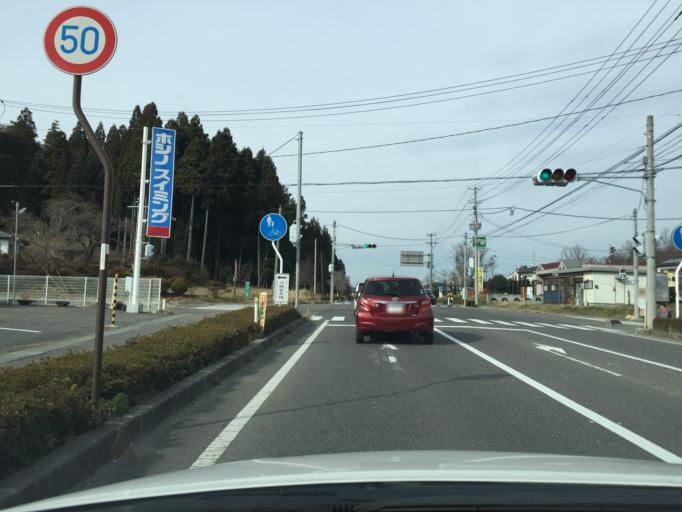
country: JP
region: Fukushima
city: Funehikimachi-funehiki
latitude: 37.4499
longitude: 140.5808
